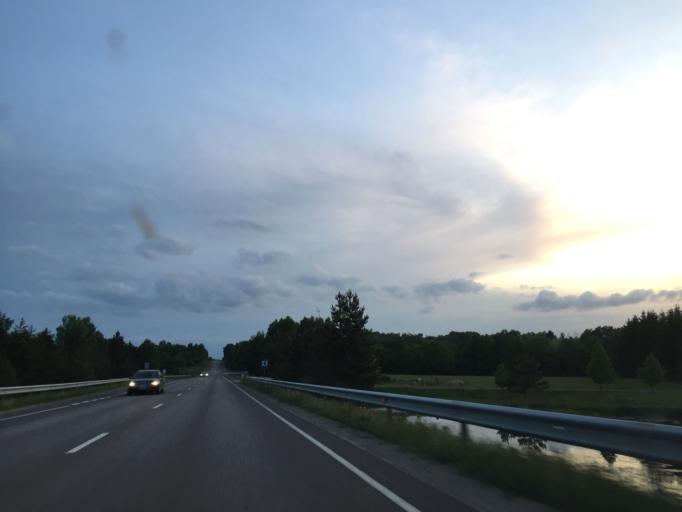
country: LT
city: Vieksniai
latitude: 55.9999
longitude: 22.5371
